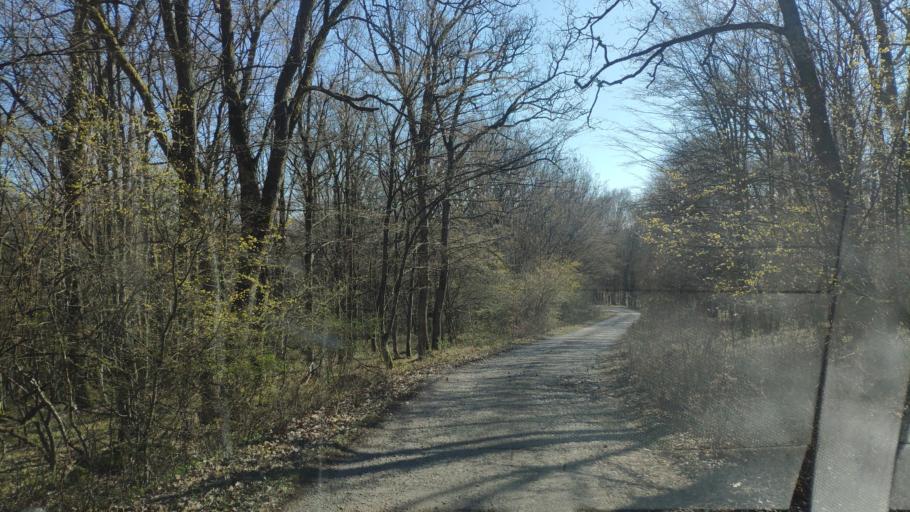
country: SK
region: Kosicky
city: Roznava
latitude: 48.5908
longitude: 20.4087
